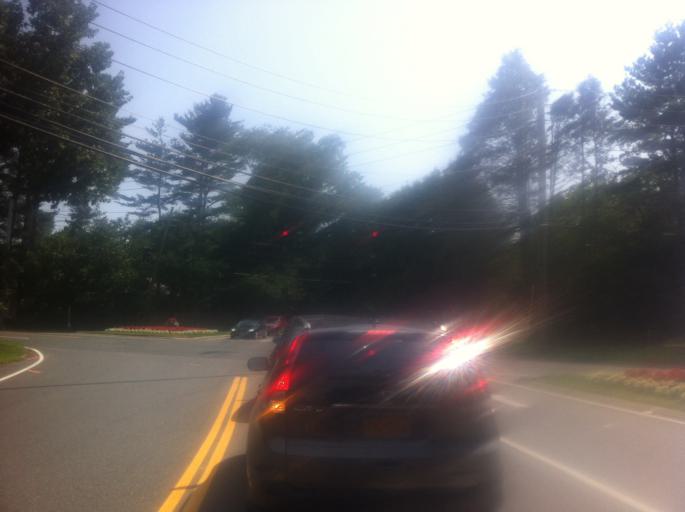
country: US
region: New York
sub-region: Nassau County
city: Brookville
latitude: 40.8180
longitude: -73.5728
